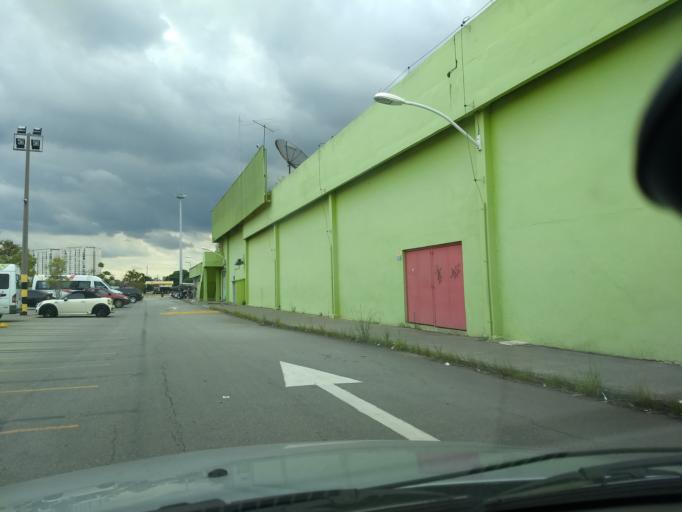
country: BR
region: Sao Paulo
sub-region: Sao Paulo
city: Sao Paulo
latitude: -23.5219
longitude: -46.5982
